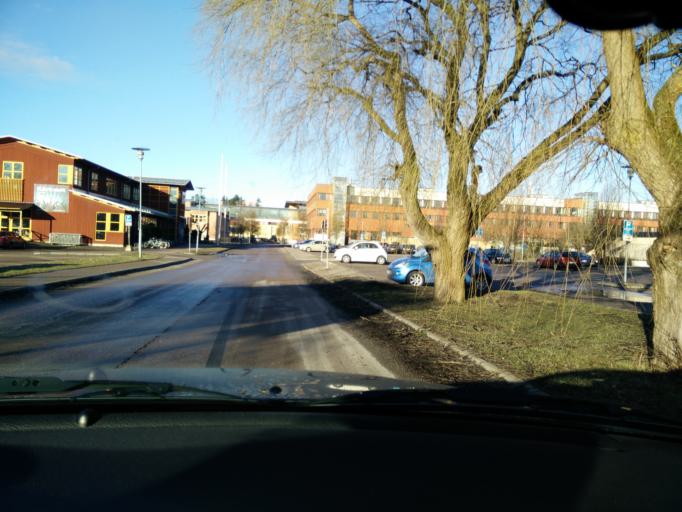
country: SE
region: Vaestmanland
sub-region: Vasteras
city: Vasteras
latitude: 59.6189
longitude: 16.5443
